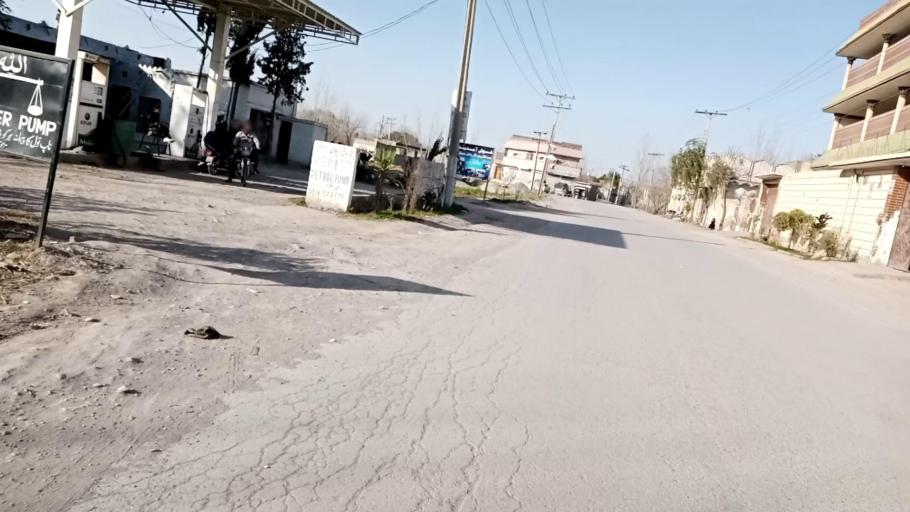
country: PK
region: Khyber Pakhtunkhwa
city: Peshawar
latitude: 34.0690
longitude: 71.5385
